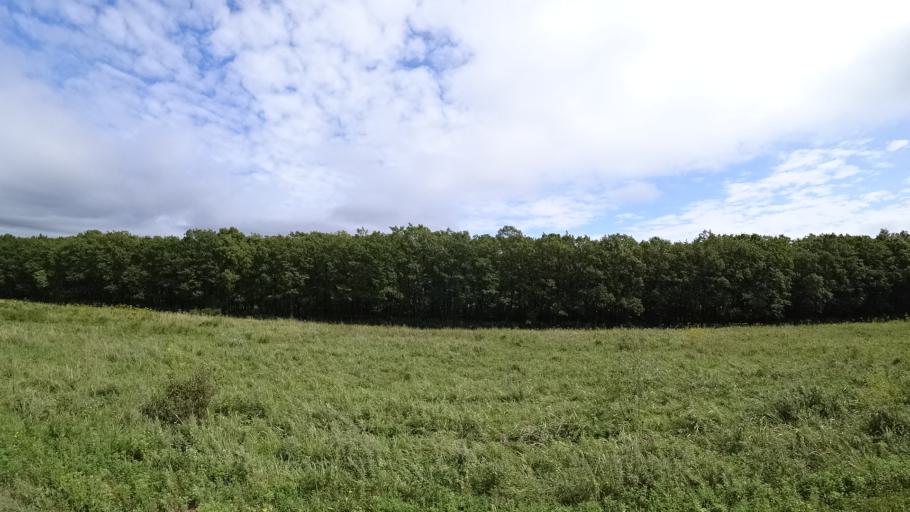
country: RU
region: Primorskiy
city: Lyalichi
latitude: 44.1454
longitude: 132.3899
